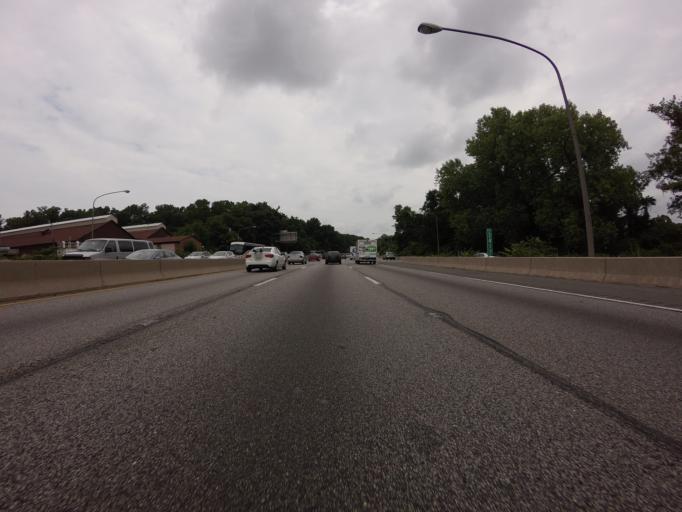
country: US
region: Pennsylvania
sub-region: Montgomery County
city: Bala-Cynwyd
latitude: 39.9886
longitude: -75.2068
